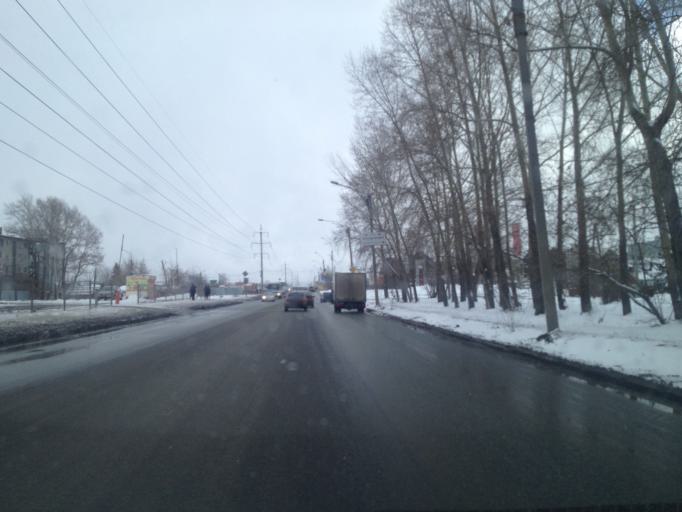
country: RU
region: Sverdlovsk
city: Sovkhoznyy
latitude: 56.7663
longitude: 60.5932
